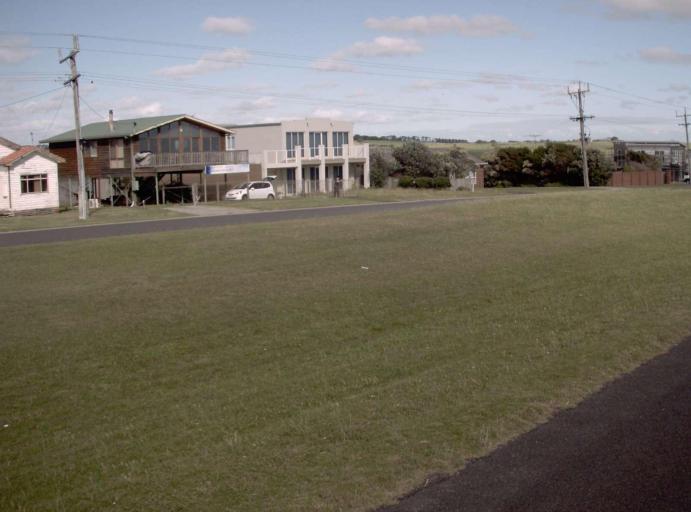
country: AU
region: Victoria
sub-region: Bass Coast
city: North Wonthaggi
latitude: -38.5518
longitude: 145.4791
